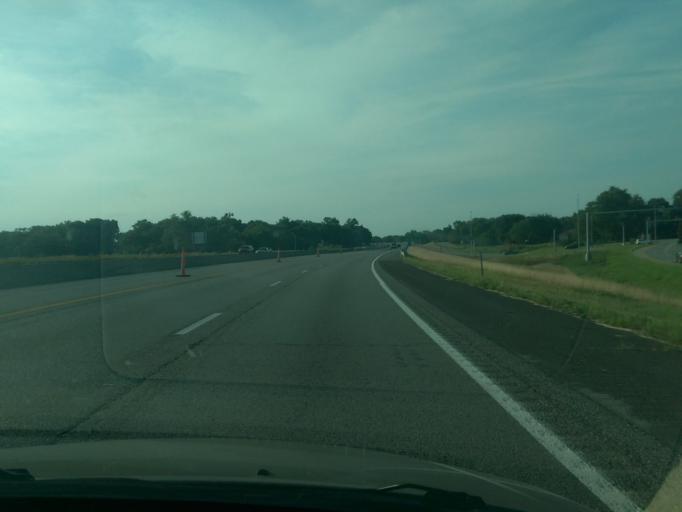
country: US
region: Missouri
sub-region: Platte County
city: Parkville
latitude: 39.2231
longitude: -94.6495
